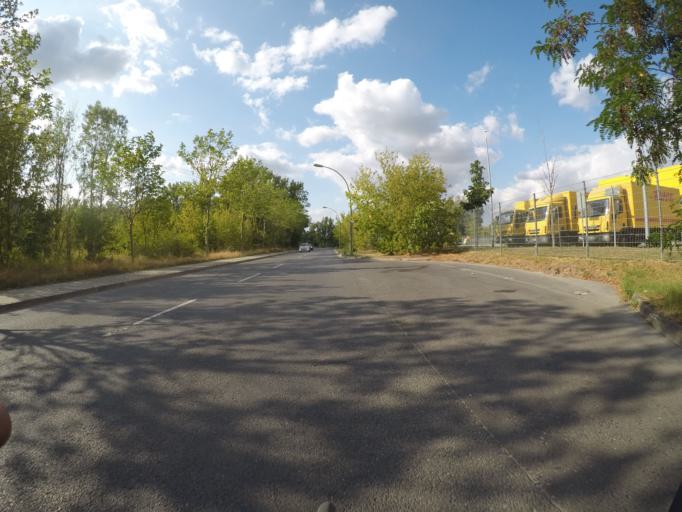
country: DE
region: Berlin
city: Alt-Hohenschoenhausen
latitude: 52.5327
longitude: 13.5268
